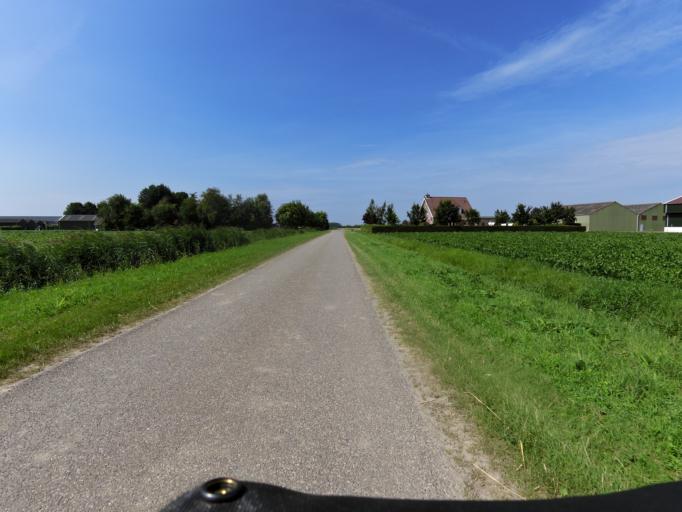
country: NL
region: North Brabant
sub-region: Gemeente Steenbergen
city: Dinteloord
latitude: 51.6920
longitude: 4.3382
